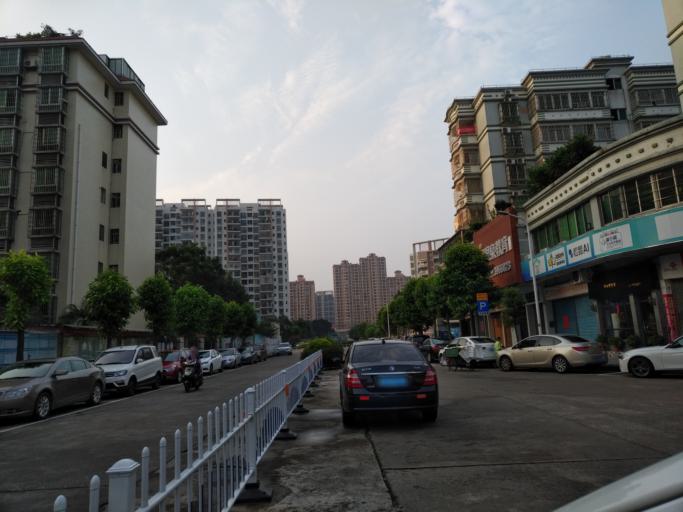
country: CN
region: Guangdong
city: Jianghai
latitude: 22.5724
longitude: 113.1090
